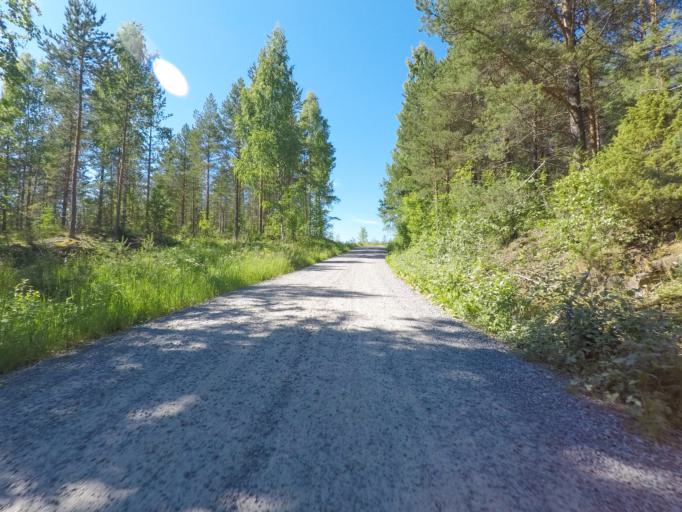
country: FI
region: Northern Savo
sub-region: Varkaus
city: Kangaslampi
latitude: 62.1781
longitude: 28.2235
